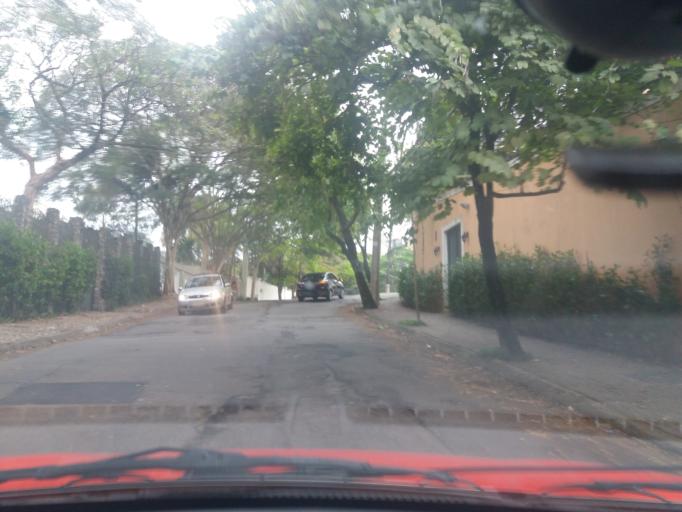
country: BR
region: Sao Paulo
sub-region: Taboao Da Serra
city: Taboao da Serra
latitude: -23.5937
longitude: -46.7145
